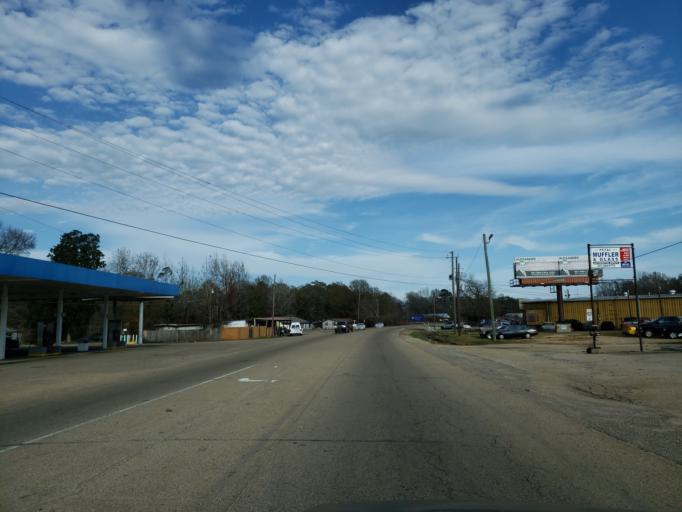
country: US
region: Mississippi
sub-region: Forrest County
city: Hattiesburg
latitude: 31.3423
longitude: -89.3013
